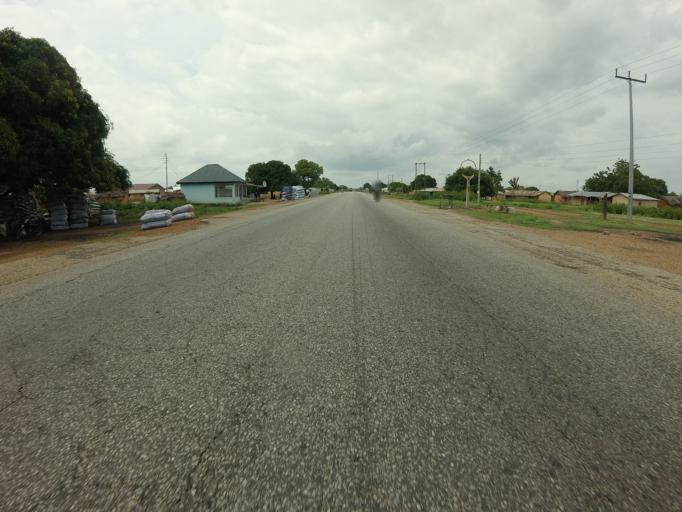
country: GH
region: Brong-Ahafo
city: Kintampo
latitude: 8.7366
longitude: -1.4712
